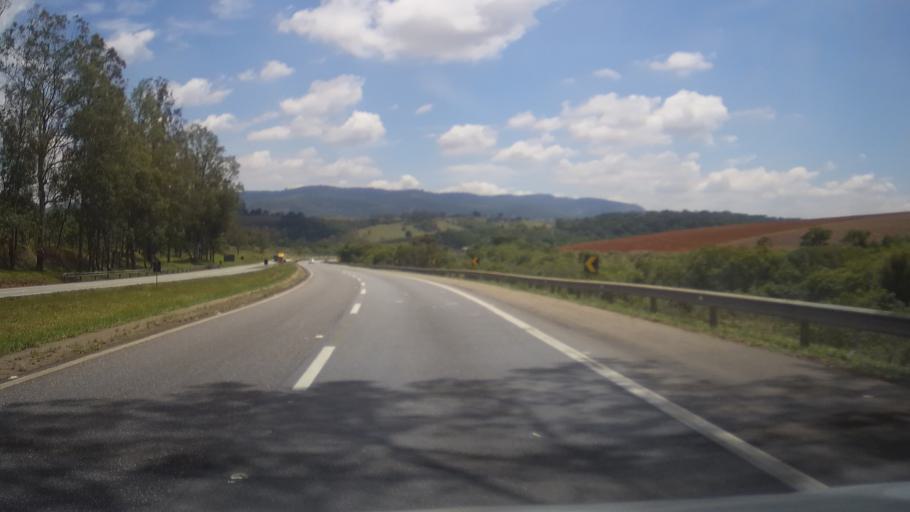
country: BR
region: Minas Gerais
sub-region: Sao Goncalo Do Sapucai
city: Sao Goncalo do Sapucai
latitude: -21.9277
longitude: -45.6114
